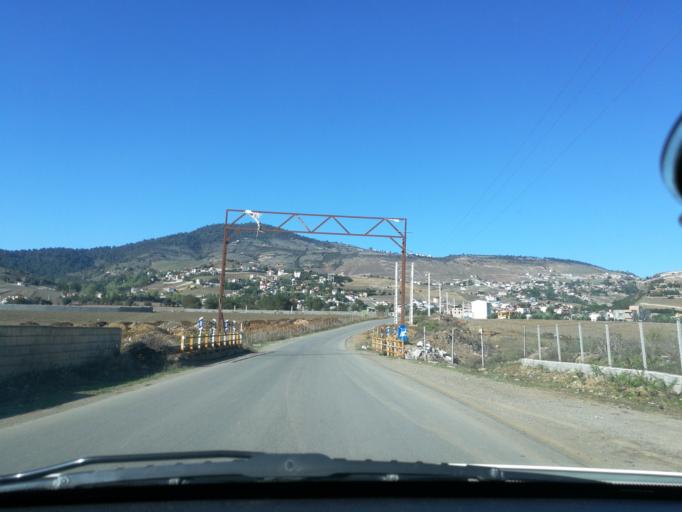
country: IR
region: Mazandaran
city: `Abbasabad
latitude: 36.5417
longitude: 51.1822
